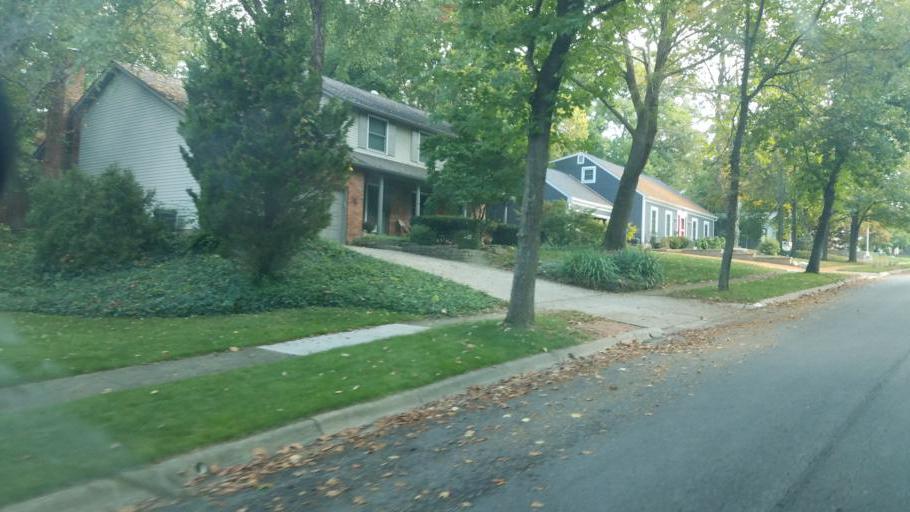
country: US
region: Ohio
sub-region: Franklin County
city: Worthington
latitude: 40.1070
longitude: -83.0313
